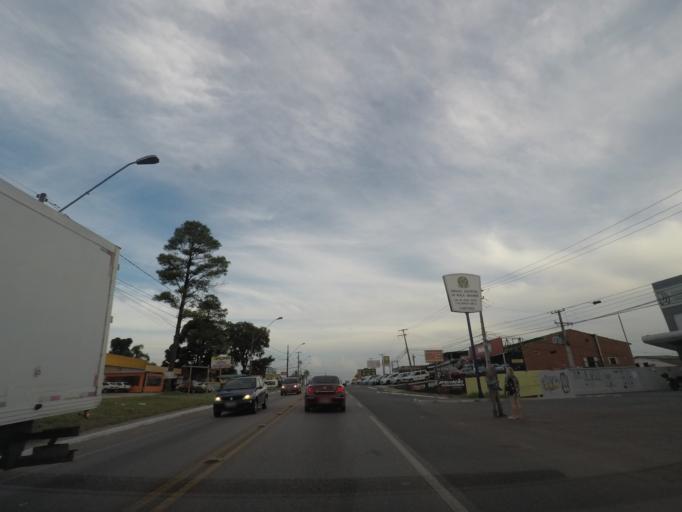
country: BR
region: Parana
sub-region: Colombo
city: Colombo
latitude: -25.3548
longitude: -49.2190
